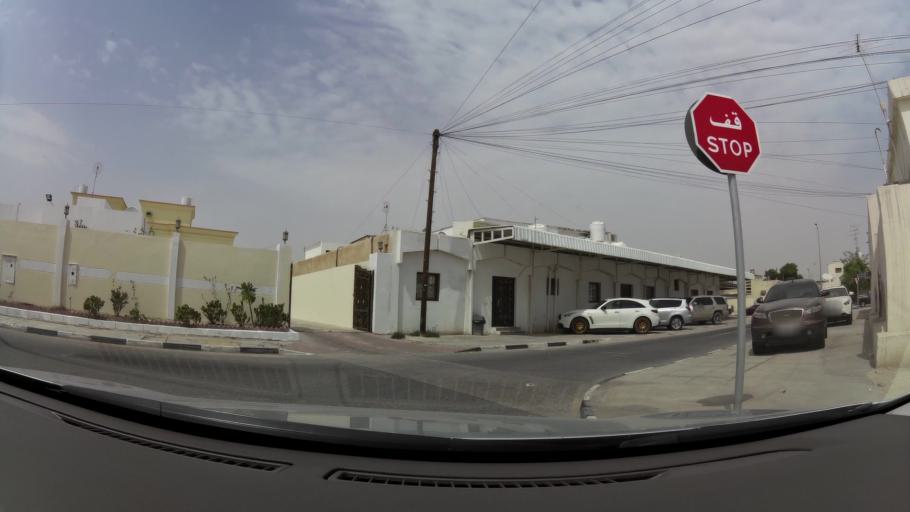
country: QA
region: Baladiyat ad Dawhah
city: Doha
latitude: 25.3107
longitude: 51.4837
